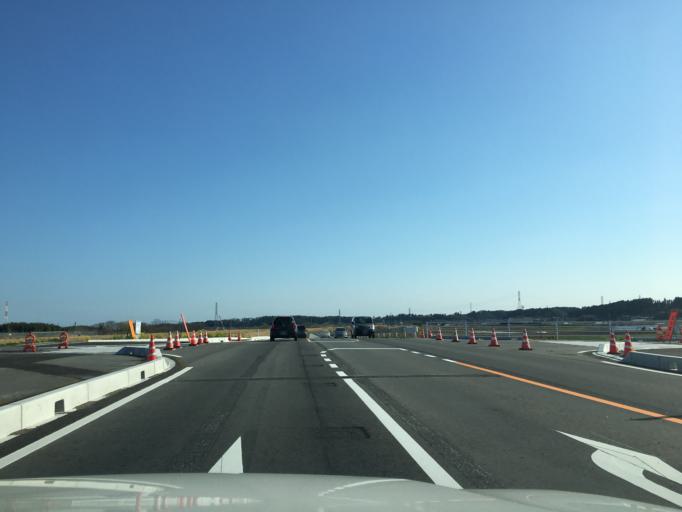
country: JP
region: Ibaraki
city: Mito-shi
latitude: 36.4337
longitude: 140.4196
